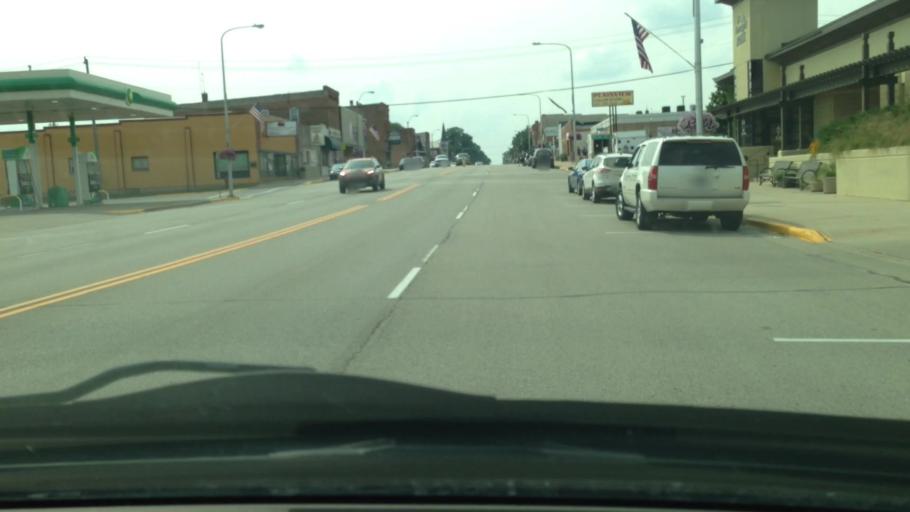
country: US
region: Minnesota
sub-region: Wabasha County
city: Plainview
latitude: 44.1650
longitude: -92.1677
